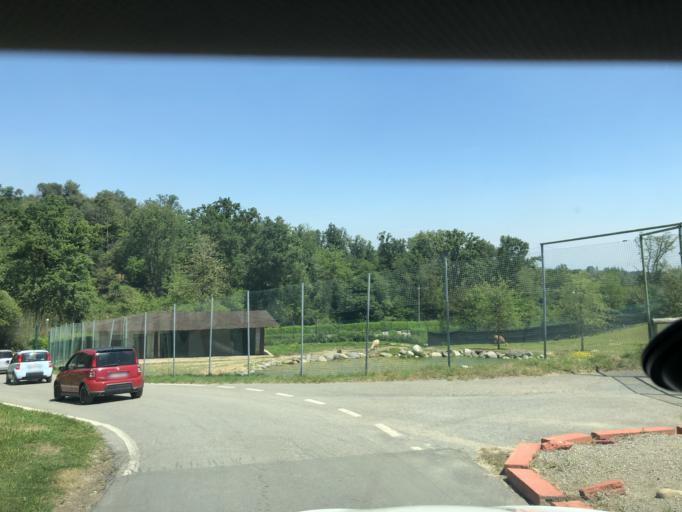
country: IT
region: Piedmont
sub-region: Provincia di Novara
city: Mezzomerico
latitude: 45.6393
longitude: 8.6134
